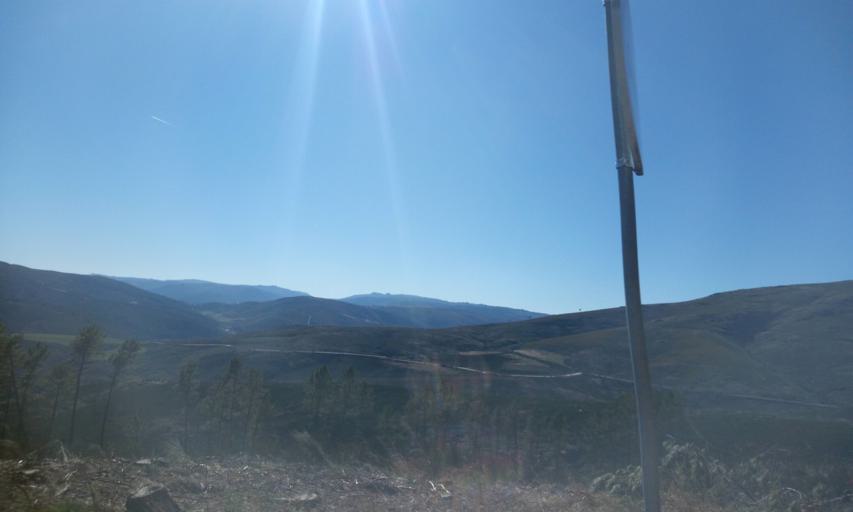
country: PT
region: Guarda
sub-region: Manteigas
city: Manteigas
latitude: 40.4730
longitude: -7.5067
